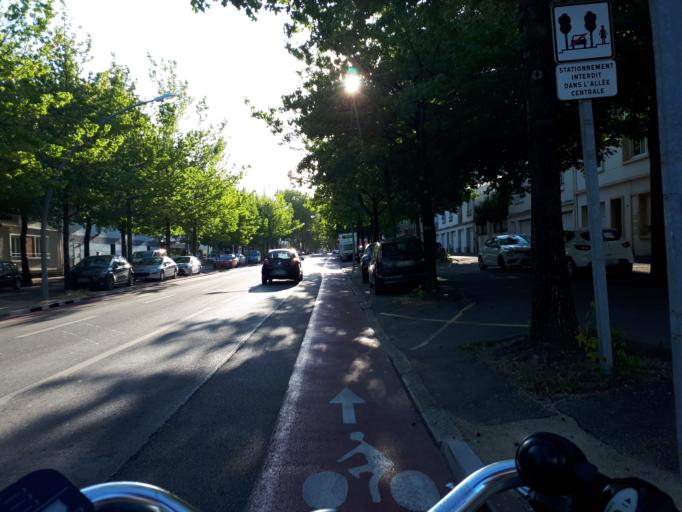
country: FR
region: Pays de la Loire
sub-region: Departement de la Loire-Atlantique
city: Saint-Nazaire
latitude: 47.2828
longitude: -2.2095
